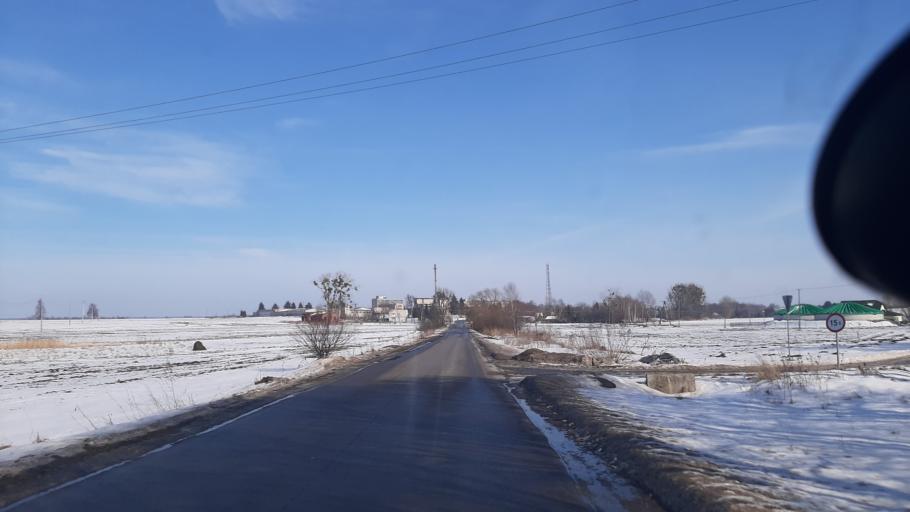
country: PL
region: Lublin Voivodeship
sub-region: Powiat pulawski
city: Kurow
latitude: 51.3824
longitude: 22.1633
